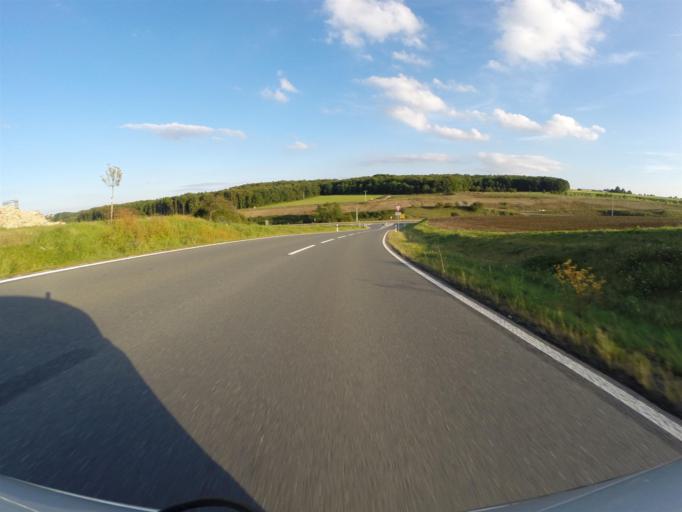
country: DE
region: Thuringia
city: Bucha
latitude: 50.8794
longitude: 11.5219
